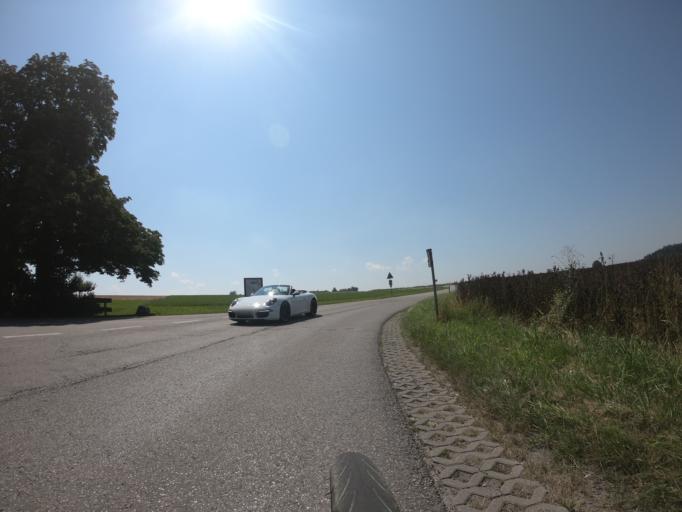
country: DE
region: Bavaria
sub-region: Upper Bavaria
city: Fuerstenfeldbruck
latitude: 48.1502
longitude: 11.2564
